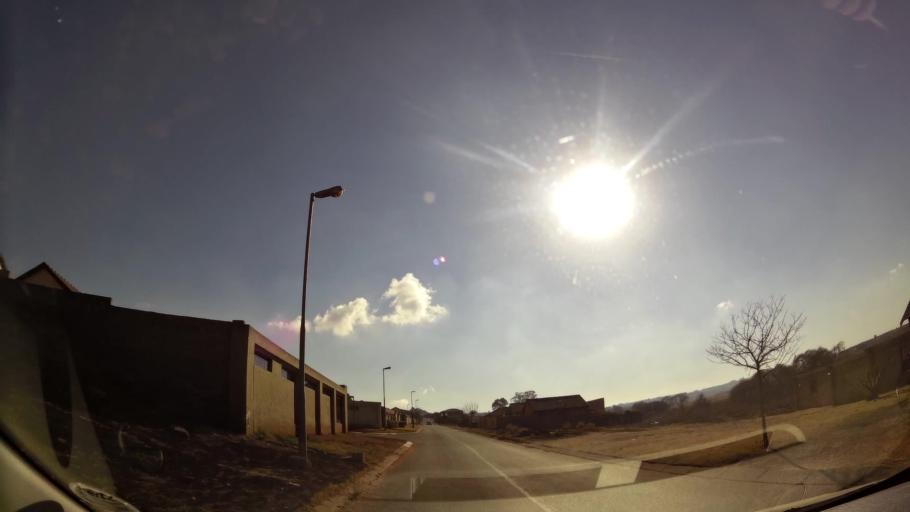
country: ZA
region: Gauteng
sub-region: City of Johannesburg Metropolitan Municipality
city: Roodepoort
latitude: -26.1621
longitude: 27.8343
